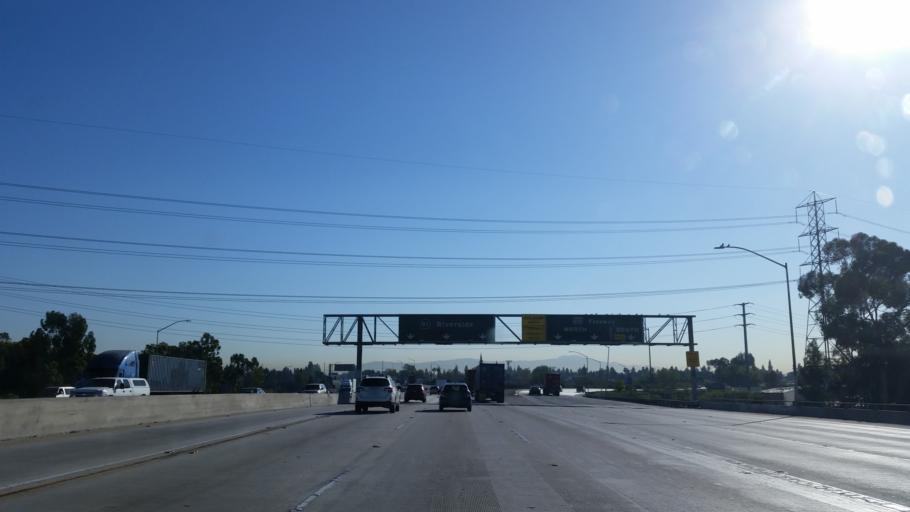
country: US
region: California
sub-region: Los Angeles County
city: Bellflower
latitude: 33.8766
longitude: -118.1079
